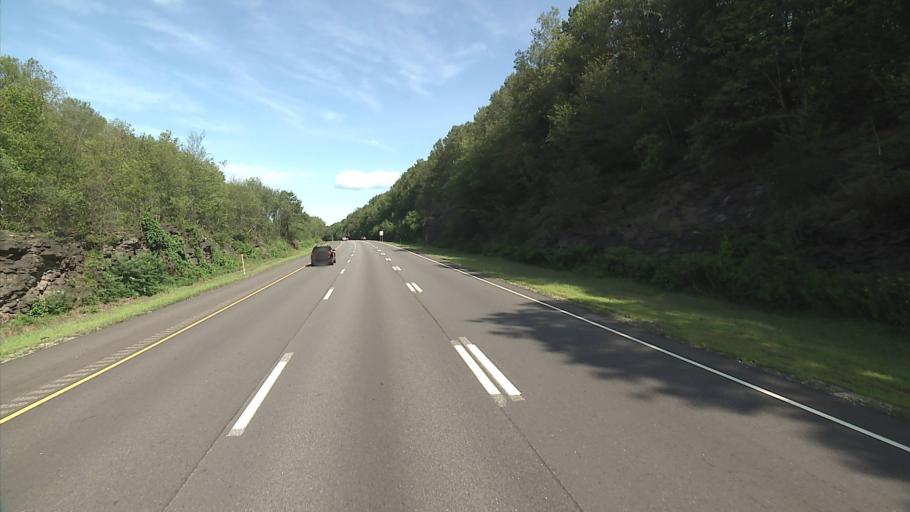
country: US
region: Connecticut
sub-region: Hartford County
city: Terramuggus
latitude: 41.6411
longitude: -72.4629
